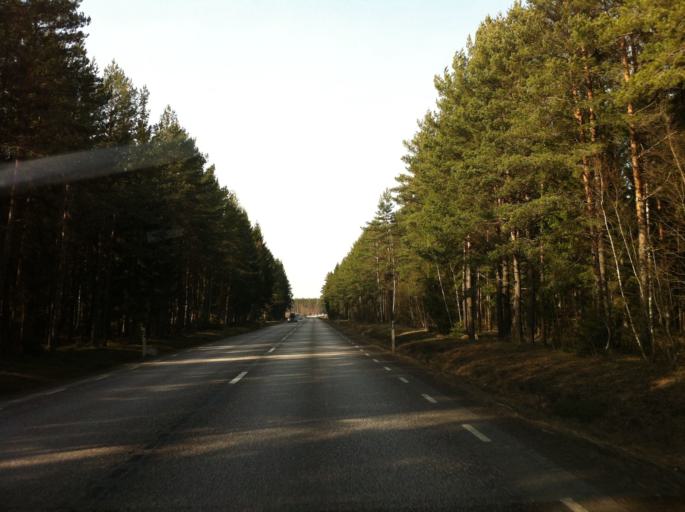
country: SE
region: Vaestra Goetaland
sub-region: Tidaholms Kommun
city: Tidaholm
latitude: 58.2088
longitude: 13.8740
